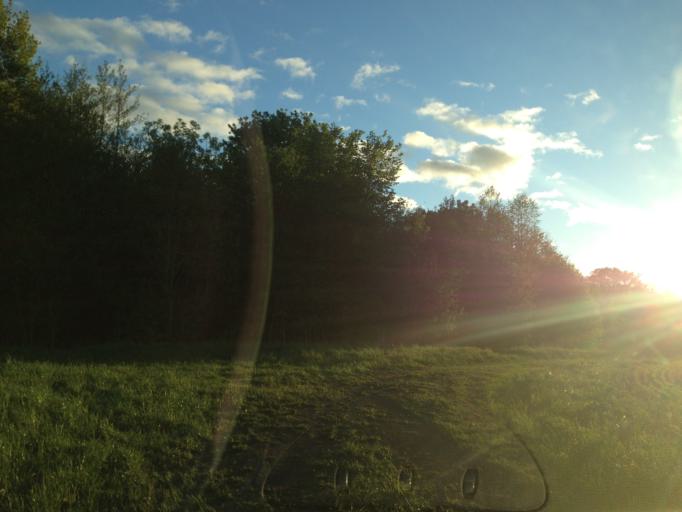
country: EE
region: Raplamaa
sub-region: Maerjamaa vald
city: Marjamaa
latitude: 58.7434
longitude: 24.1633
